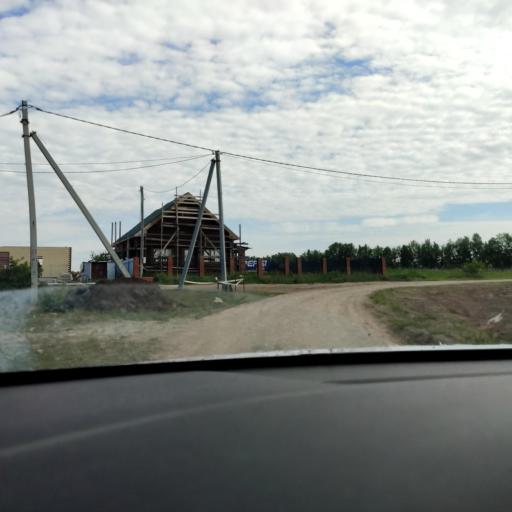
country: RU
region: Tatarstan
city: Pestretsy
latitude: 55.7126
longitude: 49.4562
